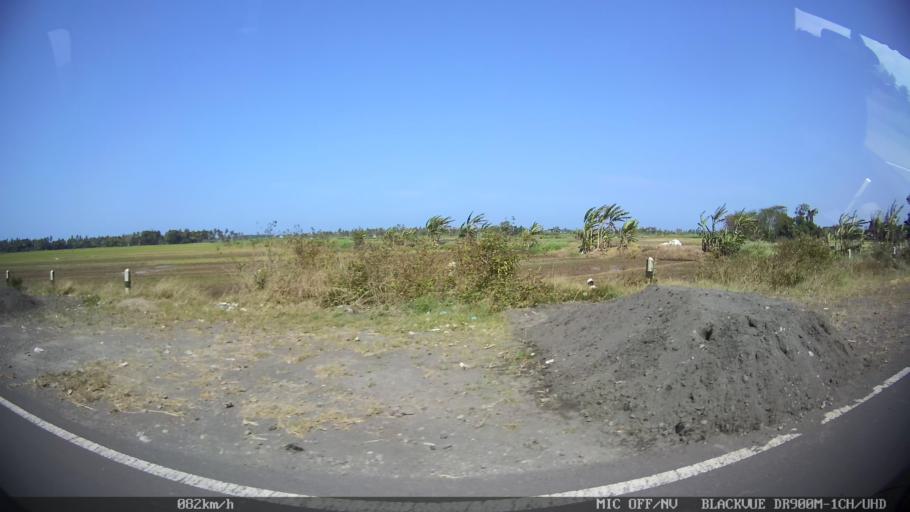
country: ID
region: Daerah Istimewa Yogyakarta
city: Srandakan
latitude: -7.9638
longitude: 110.2050
